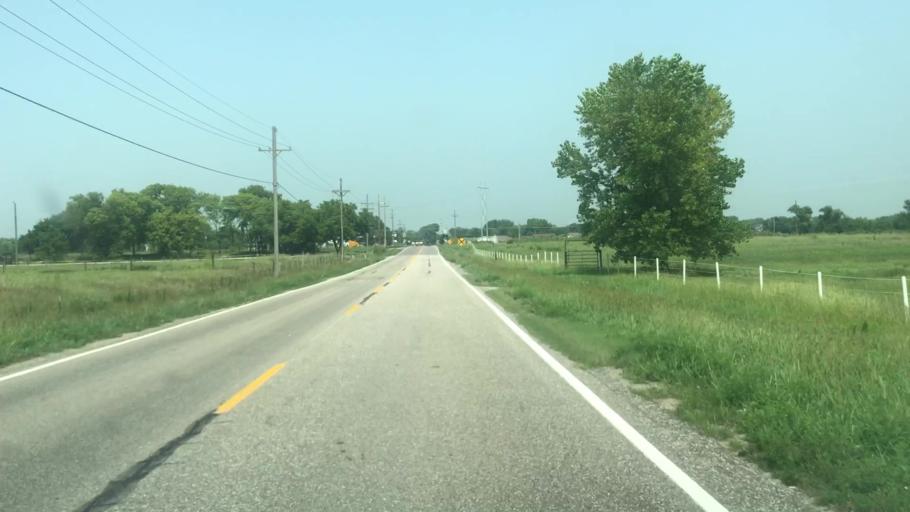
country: US
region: Nebraska
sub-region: Hall County
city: Grand Island
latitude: 40.9117
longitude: -98.3018
